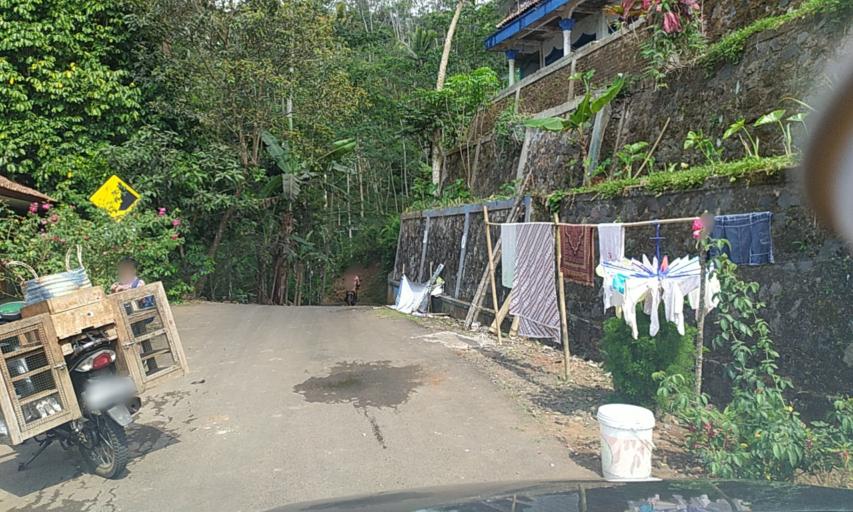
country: ID
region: Central Java
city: Kutaagung
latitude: -7.1814
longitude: 108.5727
